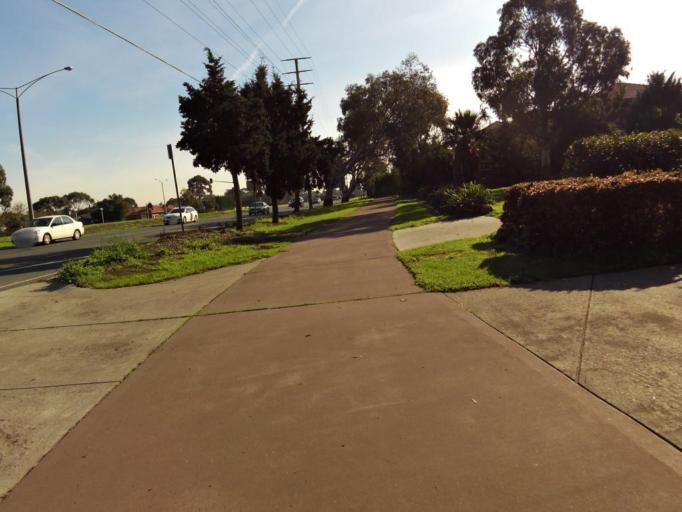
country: AU
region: Victoria
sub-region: Kingston
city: Aspendale Gardens
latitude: -38.0226
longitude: 145.1253
